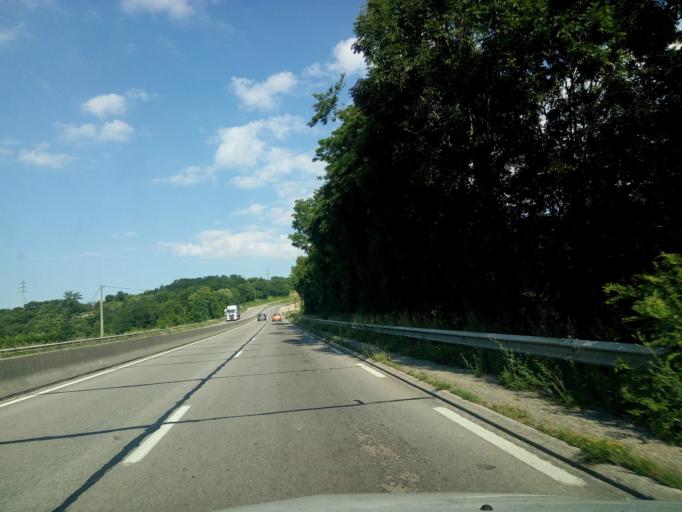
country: FR
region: Rhone-Alpes
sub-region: Departement de l'Isere
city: Moirans
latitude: 45.3365
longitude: 5.5500
